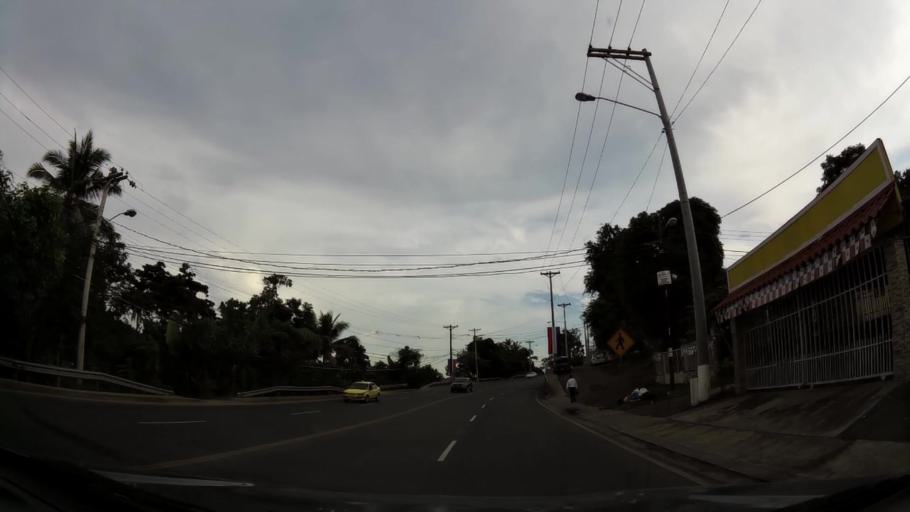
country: PA
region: Panama
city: Tocumen
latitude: 9.0932
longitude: -79.3666
